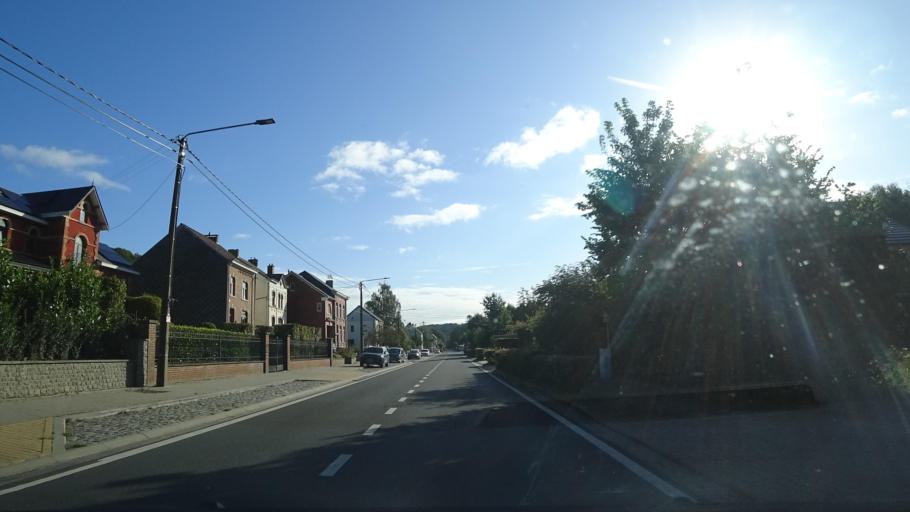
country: BE
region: Wallonia
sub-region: Province du Brabant Wallon
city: Villers-la-Ville
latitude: 50.6184
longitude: 4.5156
